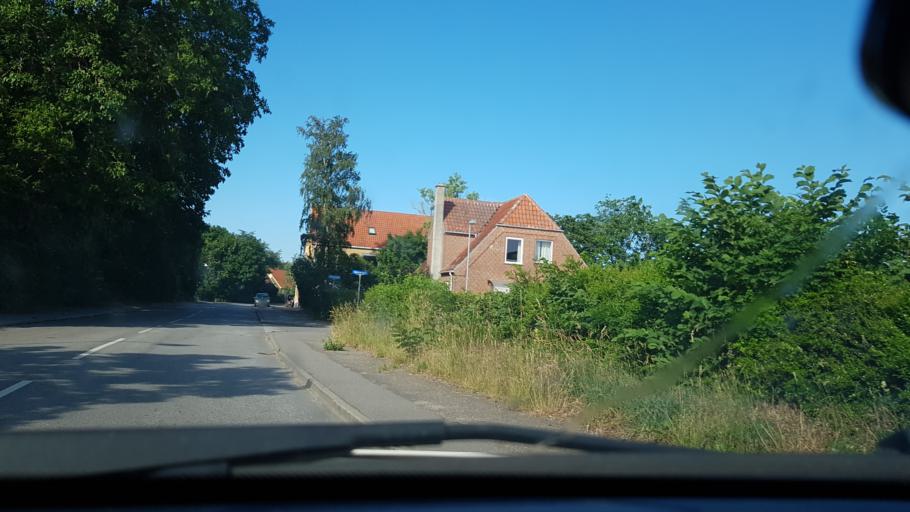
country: DK
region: Zealand
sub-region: Odsherred Kommune
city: Hojby
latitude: 55.8794
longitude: 11.6047
